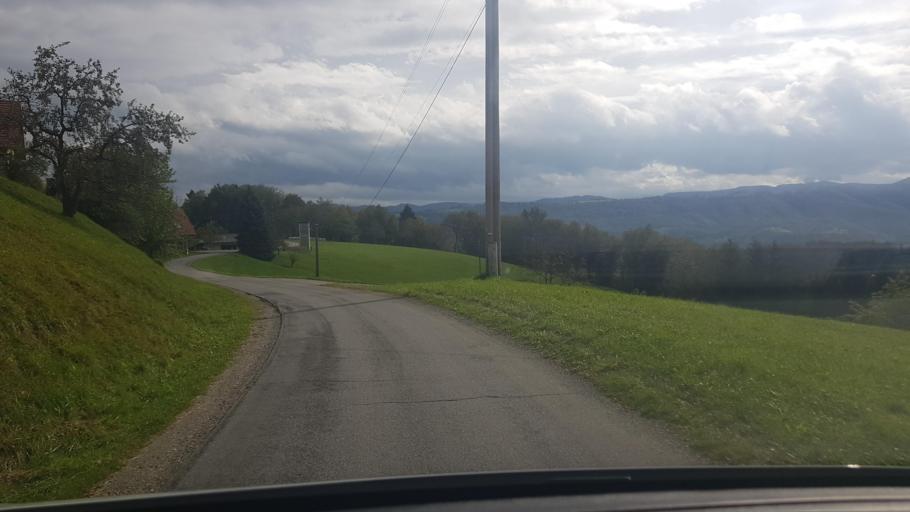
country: AT
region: Styria
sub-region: Politischer Bezirk Leibnitz
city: Sankt Johann im Saggautal
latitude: 46.6998
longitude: 15.4313
